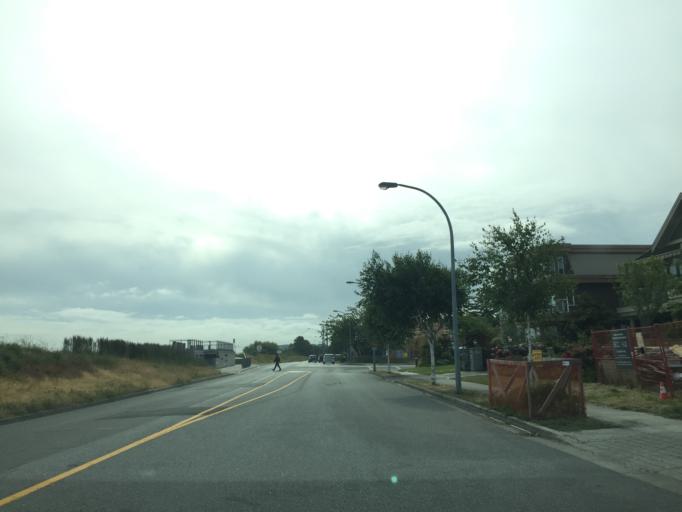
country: CA
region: British Columbia
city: Richmond
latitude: 49.1741
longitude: -123.1824
